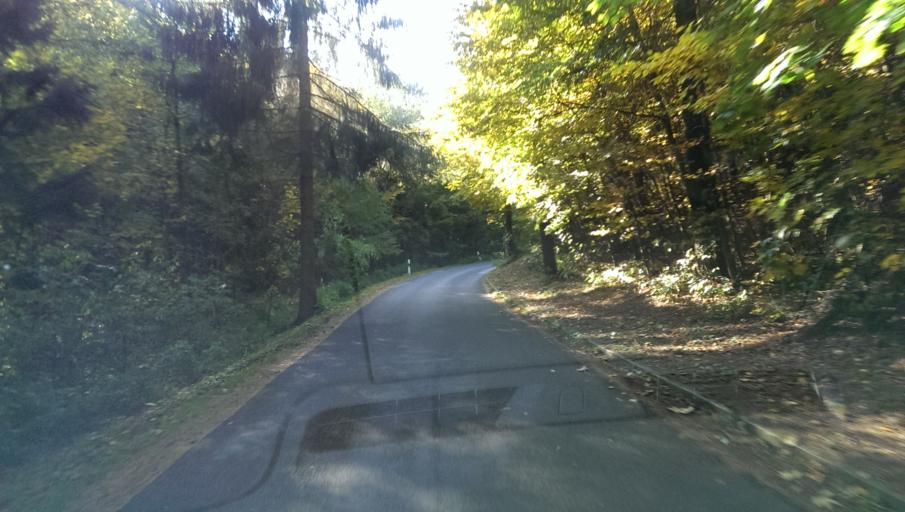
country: DE
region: Saxony
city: Liebstadt
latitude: 50.8088
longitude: 13.9056
